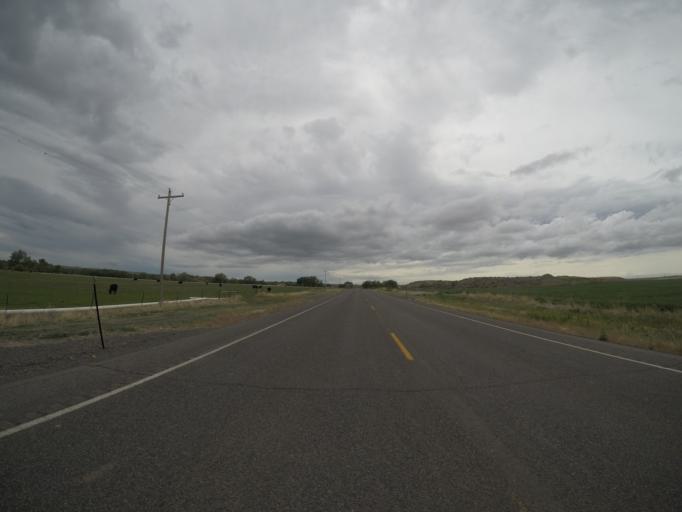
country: US
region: Wyoming
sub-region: Big Horn County
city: Lovell
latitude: 44.8704
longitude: -108.3195
